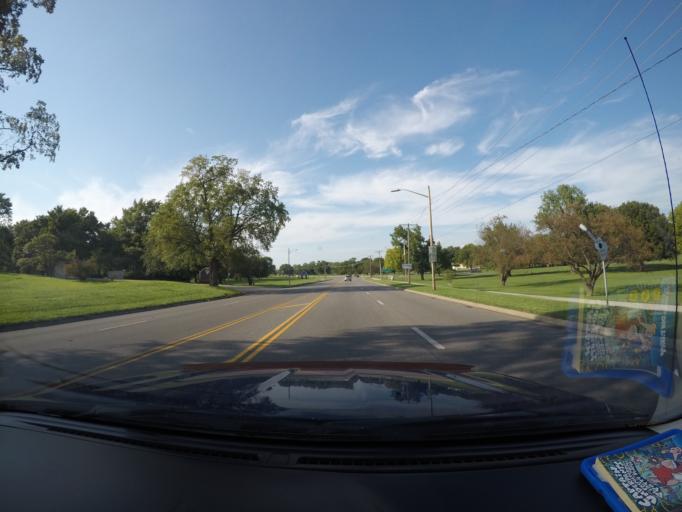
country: US
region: Kansas
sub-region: Leavenworth County
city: Lansing
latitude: 39.2757
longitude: -94.8997
